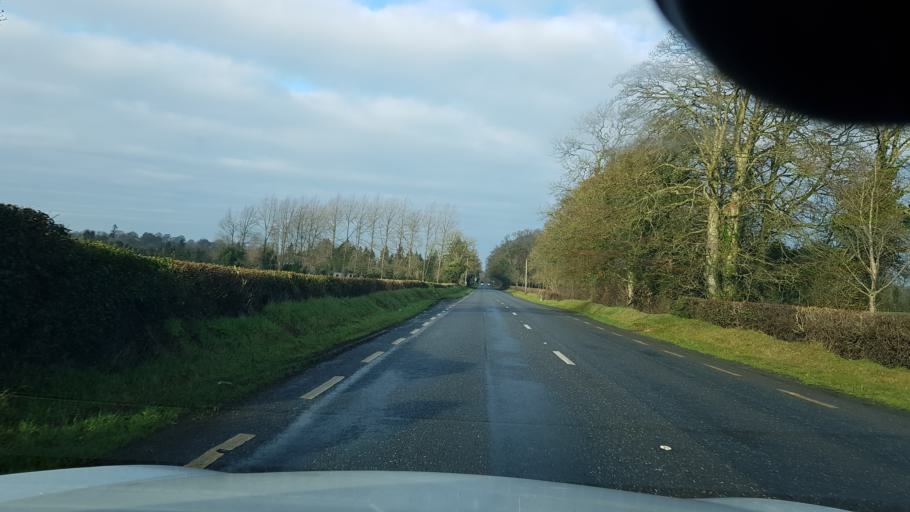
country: IE
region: Leinster
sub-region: An Mhi
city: Navan
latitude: 53.6253
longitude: -6.6518
